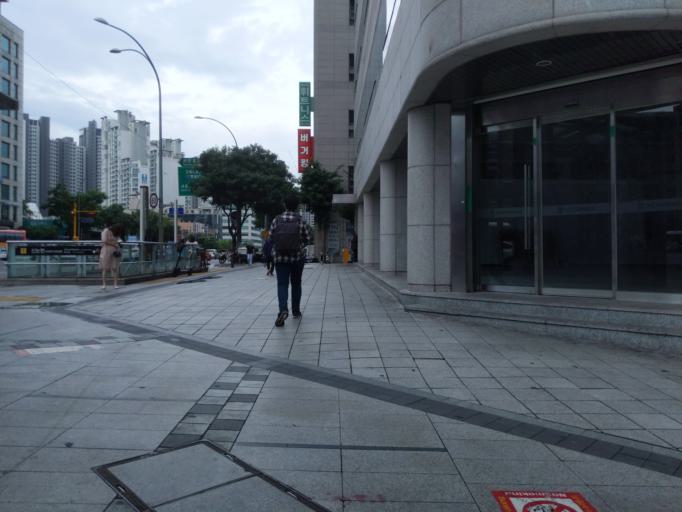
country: KR
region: Seoul
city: Seoul
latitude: 37.5046
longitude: 127.0243
